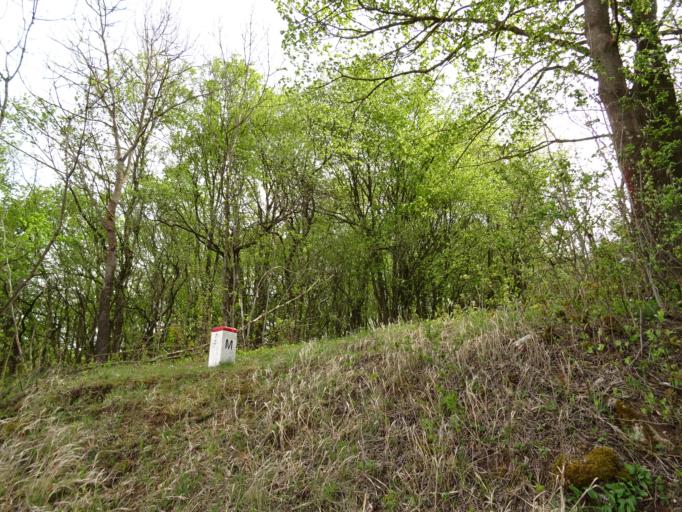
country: SK
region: Kosicky
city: Medzev
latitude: 48.5662
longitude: 20.8551
